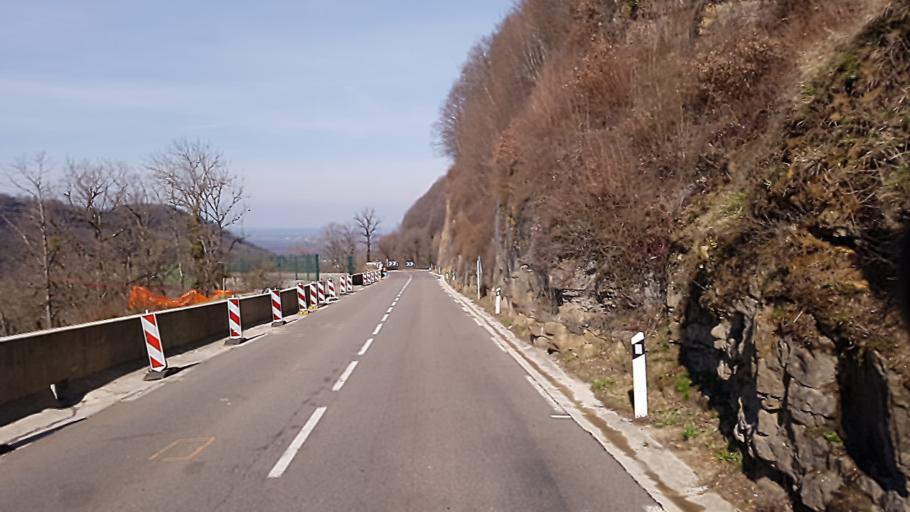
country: FR
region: Franche-Comte
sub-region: Departement du Jura
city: Poligny
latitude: 46.8211
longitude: 5.7359
